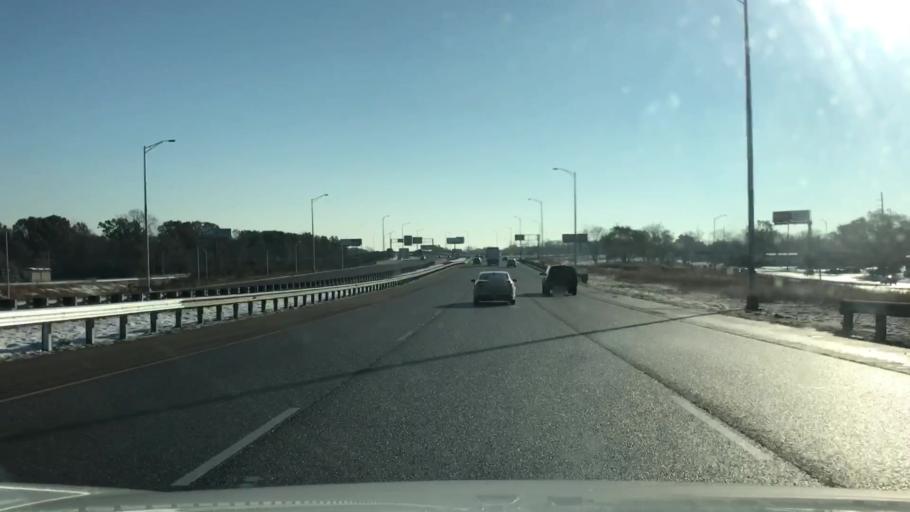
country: US
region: Illinois
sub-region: Saint Clair County
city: East Saint Louis
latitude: 38.6225
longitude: -90.1268
